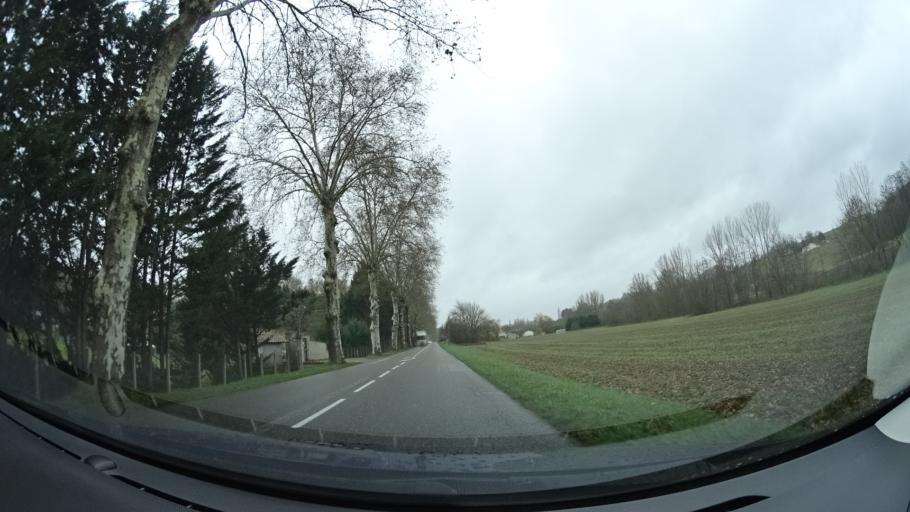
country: FR
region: Midi-Pyrenees
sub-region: Departement du Tarn-et-Garonne
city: Moissac
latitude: 44.1370
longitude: 1.1009
